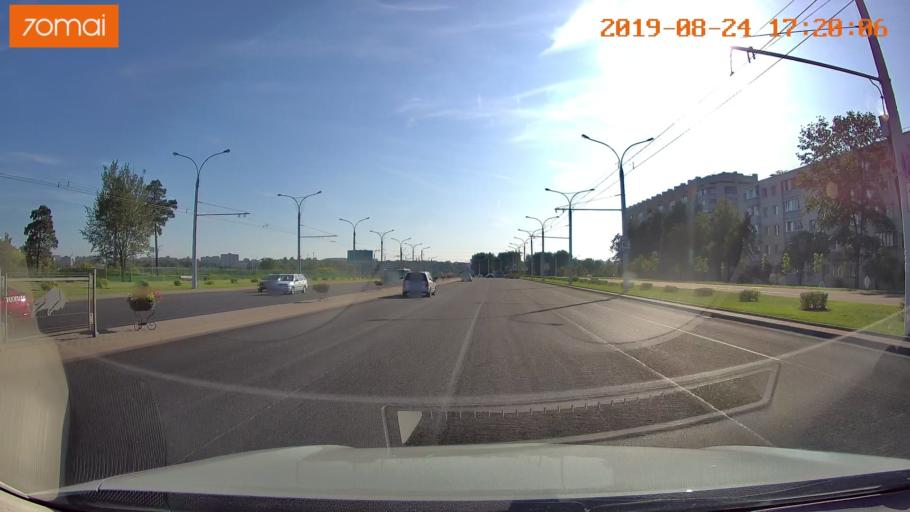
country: BY
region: Minsk
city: Hatava
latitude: 53.8568
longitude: 27.6383
